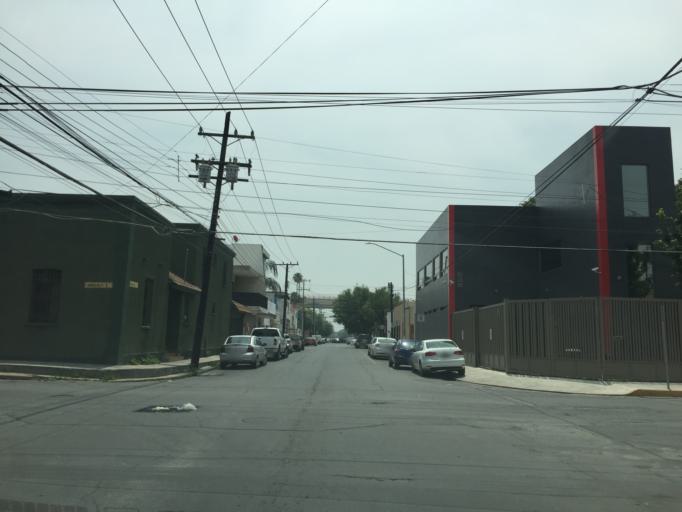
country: MX
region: Nuevo Leon
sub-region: Monterrey
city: Monterrey
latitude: 25.6798
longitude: -100.2995
